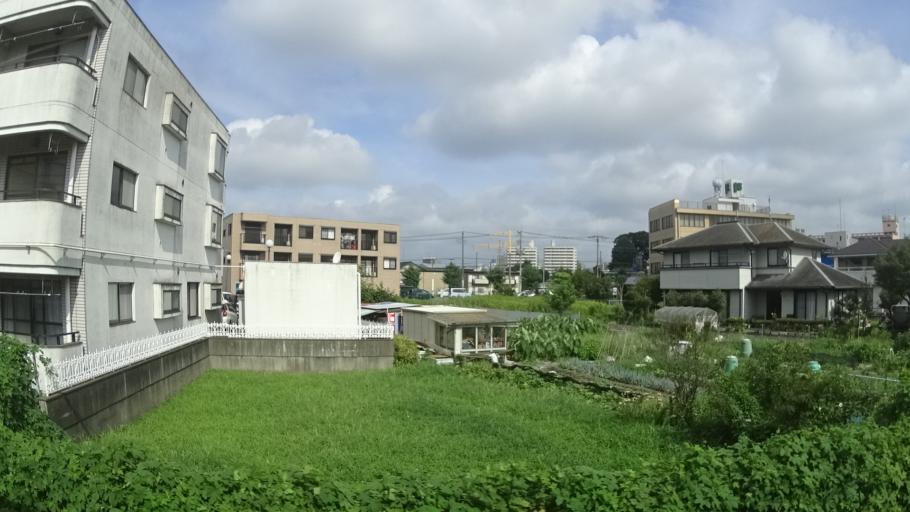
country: JP
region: Tochigi
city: Utsunomiya-shi
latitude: 36.5497
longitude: 139.8929
